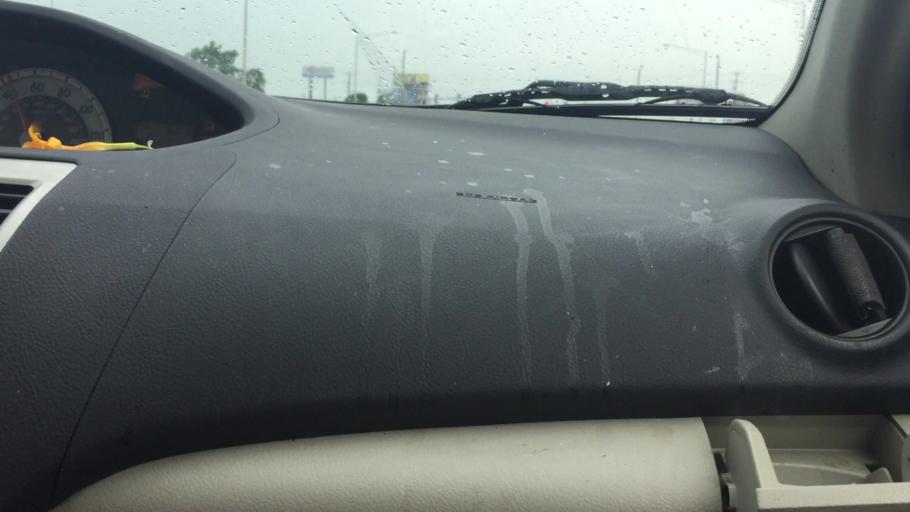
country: US
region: Illinois
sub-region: Williamson County
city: Marion
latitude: 37.7407
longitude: -88.9483
